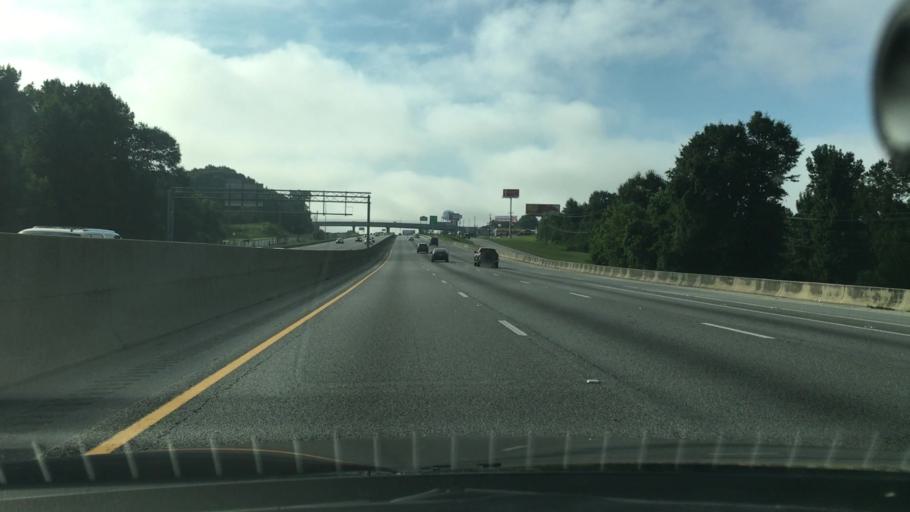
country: US
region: Georgia
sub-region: Rockdale County
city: Conyers
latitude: 33.6627
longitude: -84.0263
